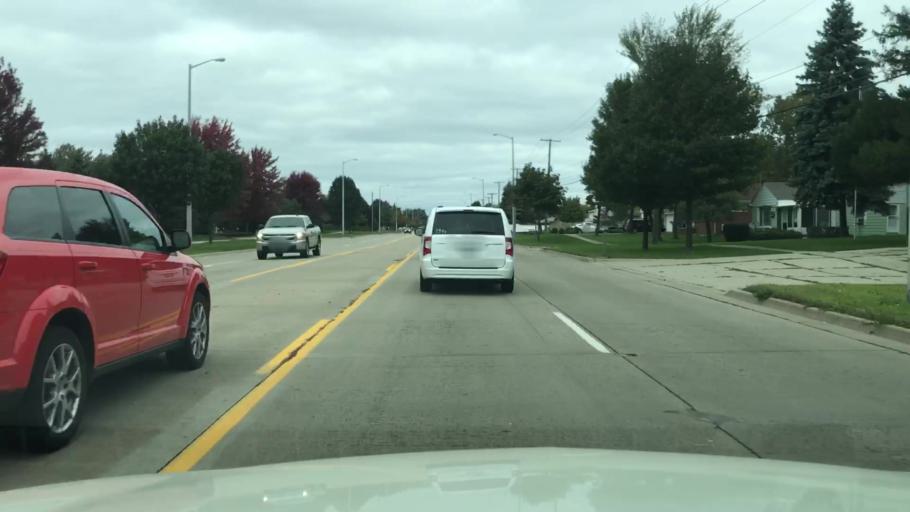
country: US
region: Michigan
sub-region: Macomb County
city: Sterling Heights
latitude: 42.5658
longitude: -83.0699
